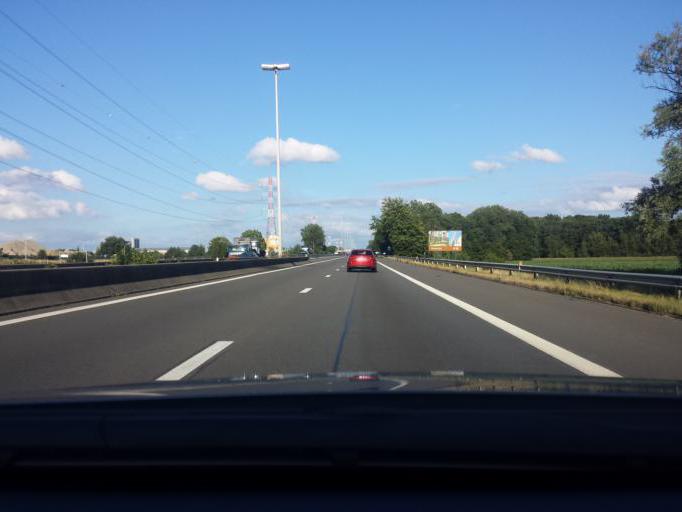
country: BE
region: Flanders
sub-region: Provincie Antwerpen
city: Grobbendonk
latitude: 51.1796
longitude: 4.7147
